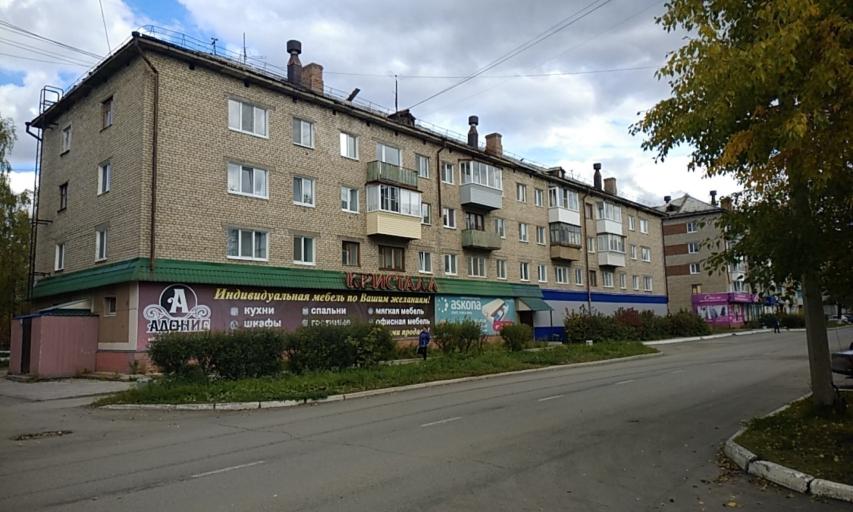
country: RU
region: Sverdlovsk
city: Krasnoural'sk
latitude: 58.3562
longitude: 60.0414
